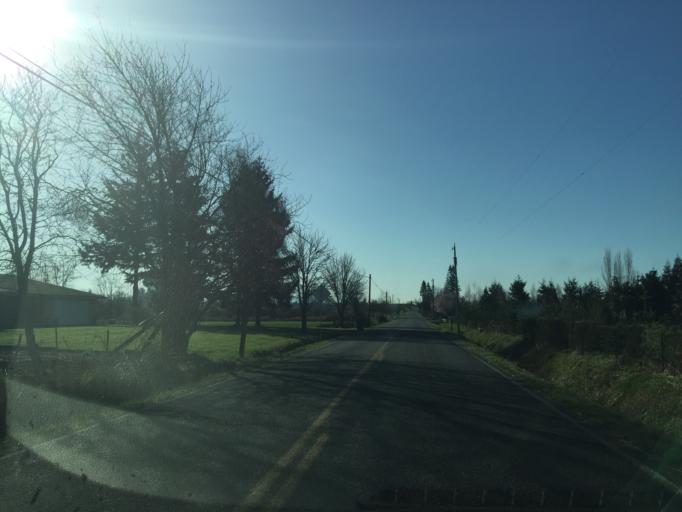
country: US
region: Washington
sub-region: Whatcom County
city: Marietta-Alderwood
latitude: 48.8473
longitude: -122.5191
